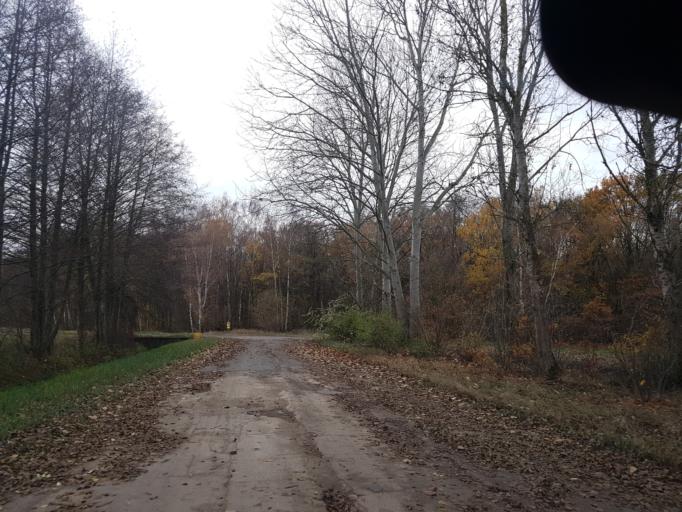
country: DE
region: Brandenburg
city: Treuenbrietzen
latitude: 52.0927
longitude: 12.9323
